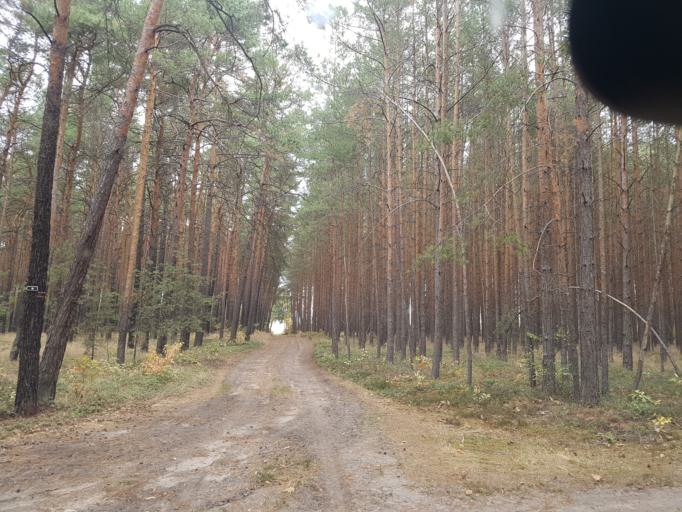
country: DE
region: Brandenburg
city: Finsterwalde
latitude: 51.5960
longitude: 13.6963
